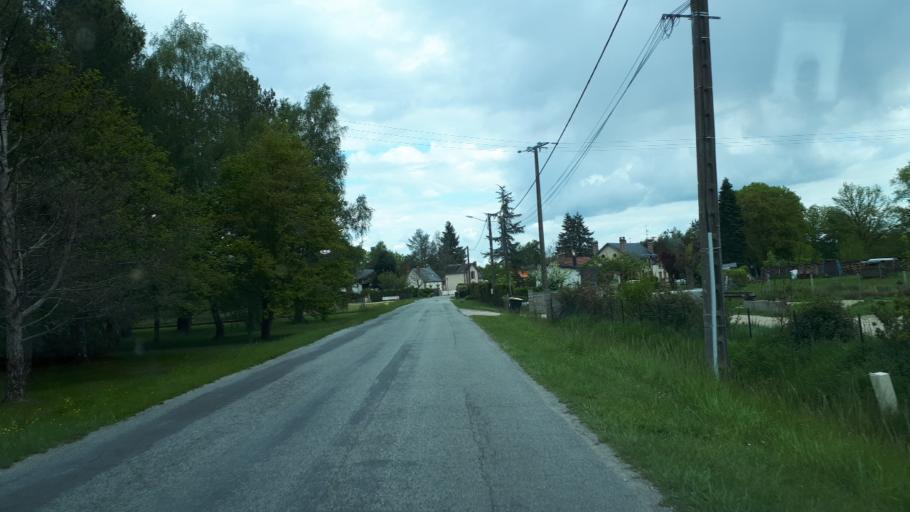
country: FR
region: Centre
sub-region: Departement du Loir-et-Cher
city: Souesmes
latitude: 47.5154
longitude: 2.1450
